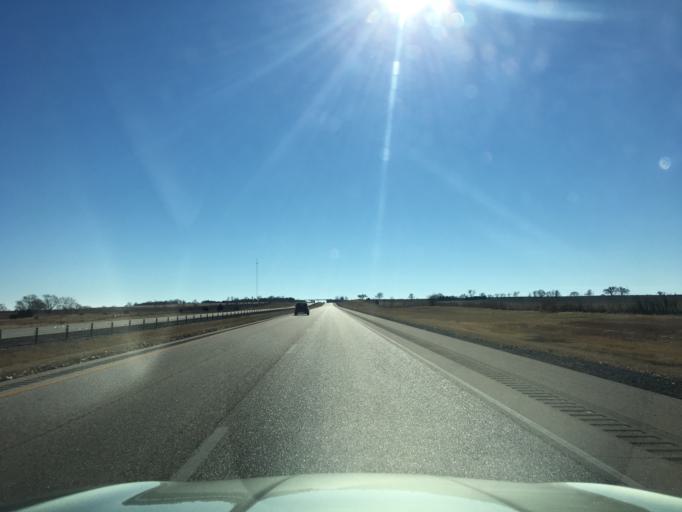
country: US
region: Oklahoma
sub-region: Kay County
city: Blackwell
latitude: 36.8798
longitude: -97.3511
